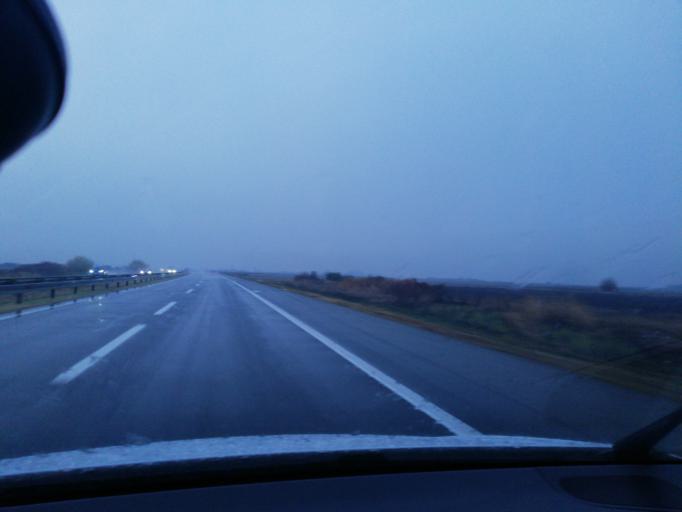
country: RS
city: Sasinci
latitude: 44.9955
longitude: 19.6953
